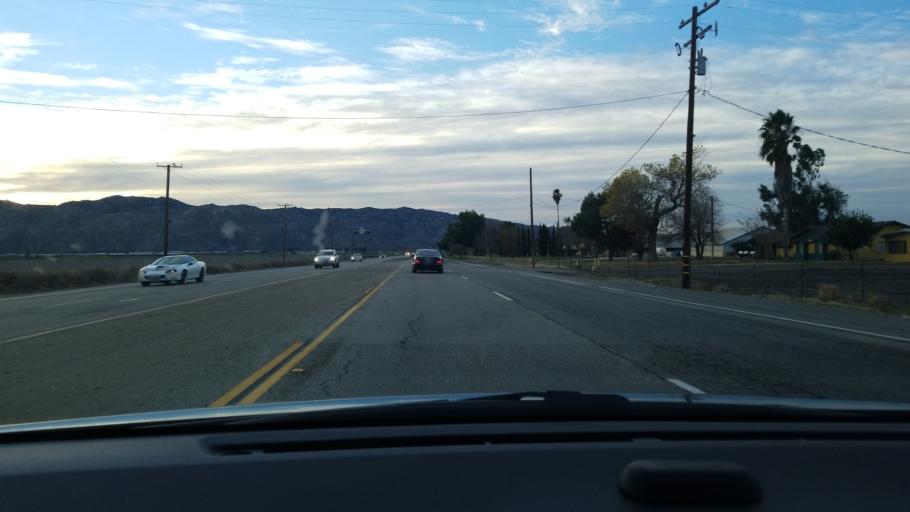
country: US
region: California
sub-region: Riverside County
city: San Jacinto
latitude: 33.8236
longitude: -117.0073
